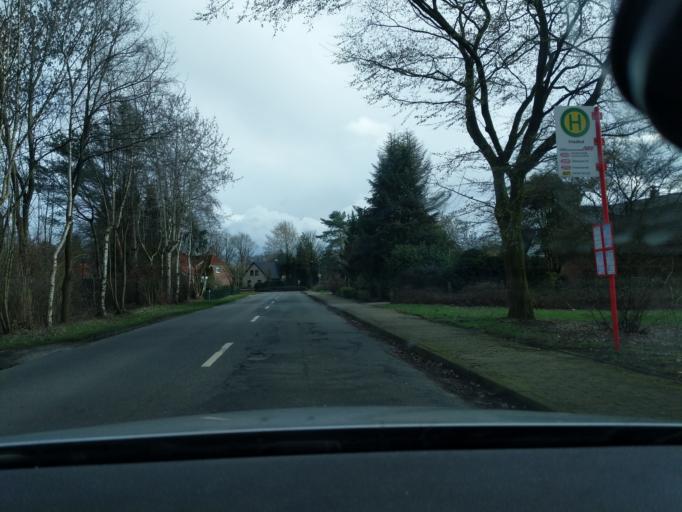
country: DE
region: Lower Saxony
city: Heinbockel
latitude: 53.5748
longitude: 9.3216
